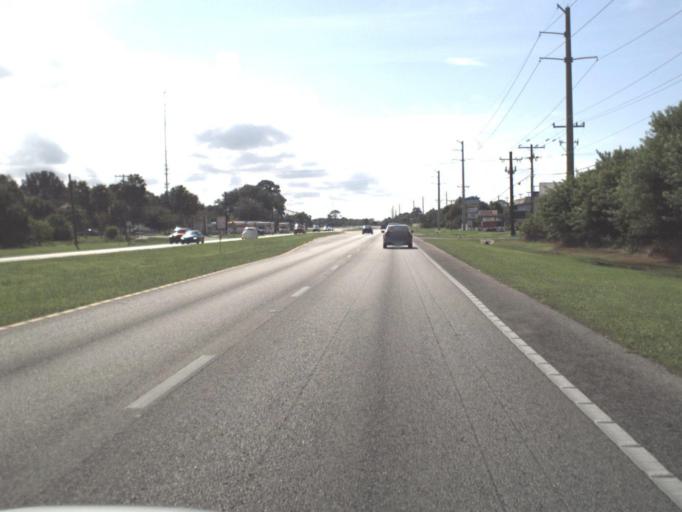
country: US
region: Florida
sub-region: Sarasota County
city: Laurel
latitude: 27.1576
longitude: -82.4709
